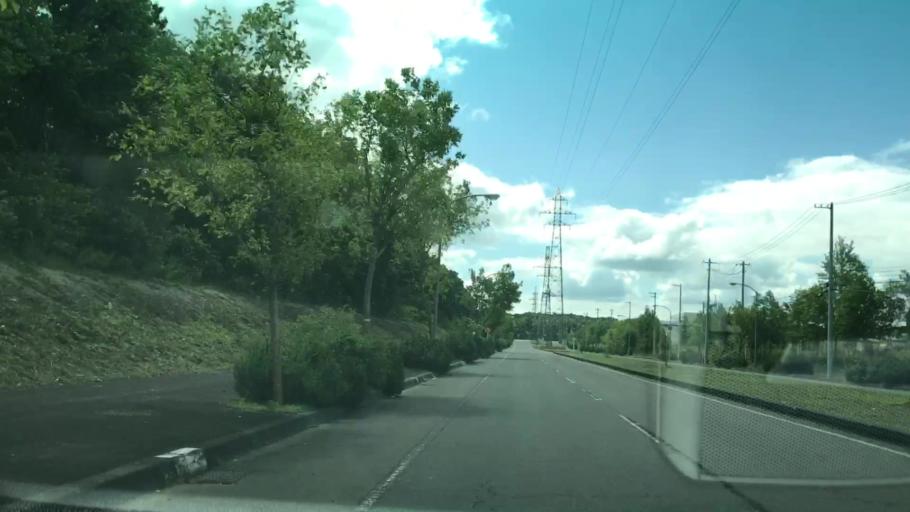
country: JP
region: Hokkaido
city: Chitose
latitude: 42.7770
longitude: 141.6166
